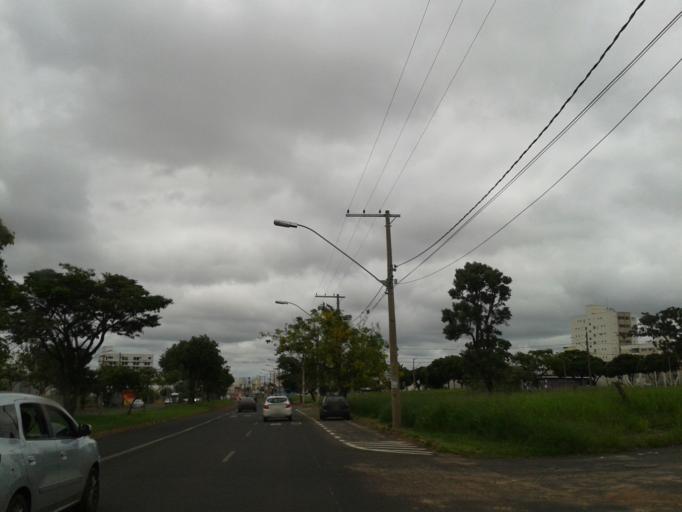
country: BR
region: Minas Gerais
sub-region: Uberlandia
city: Uberlandia
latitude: -18.9322
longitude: -48.2363
